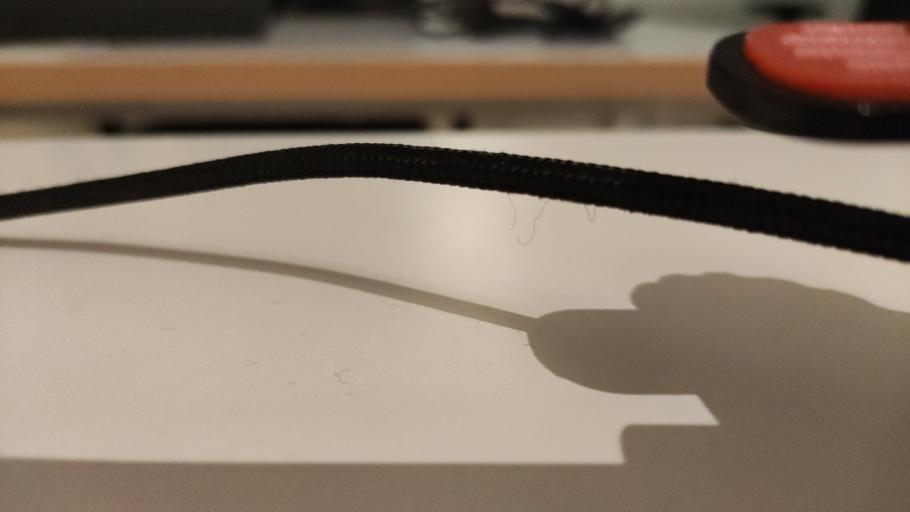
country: RU
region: Moskovskaya
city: Novoye
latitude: 55.6634
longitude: 38.9420
